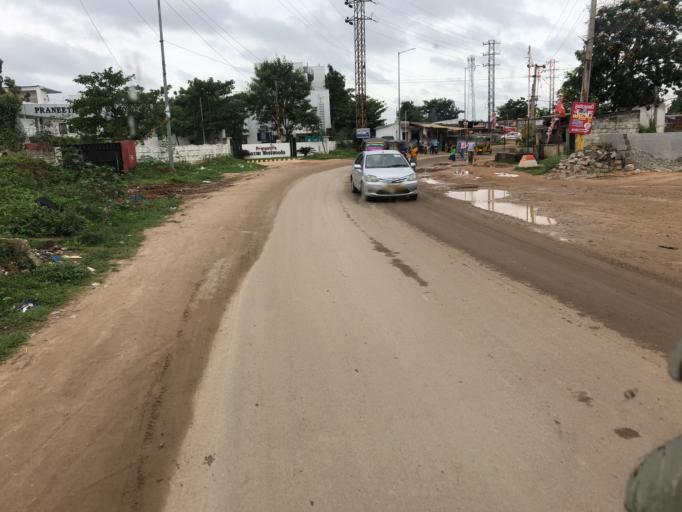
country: IN
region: Telangana
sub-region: Medak
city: Serilingampalle
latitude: 17.4421
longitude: 78.3051
